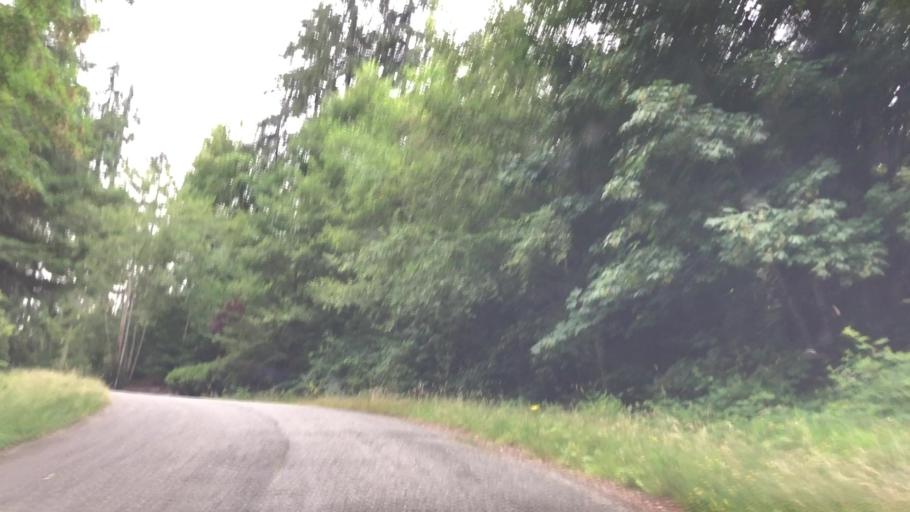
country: US
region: Washington
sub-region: King County
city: Cottage Lake
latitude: 47.7232
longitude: -122.0878
